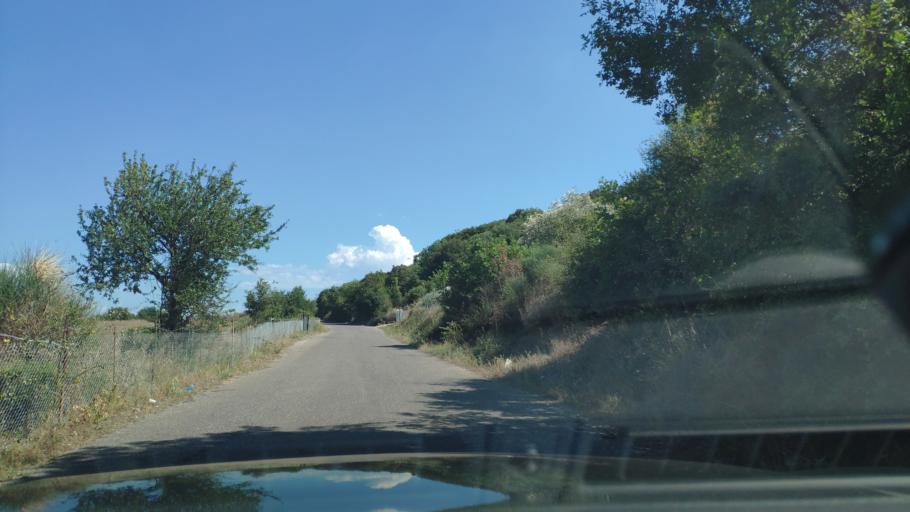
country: GR
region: West Greece
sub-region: Nomos Aitolias kai Akarnanias
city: Katouna
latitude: 38.8023
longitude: 21.1114
